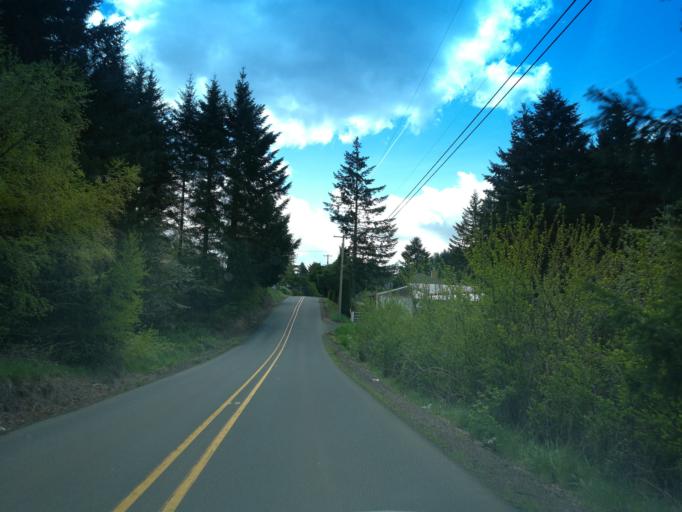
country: US
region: Oregon
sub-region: Clackamas County
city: Damascus
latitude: 45.4309
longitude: -122.4481
